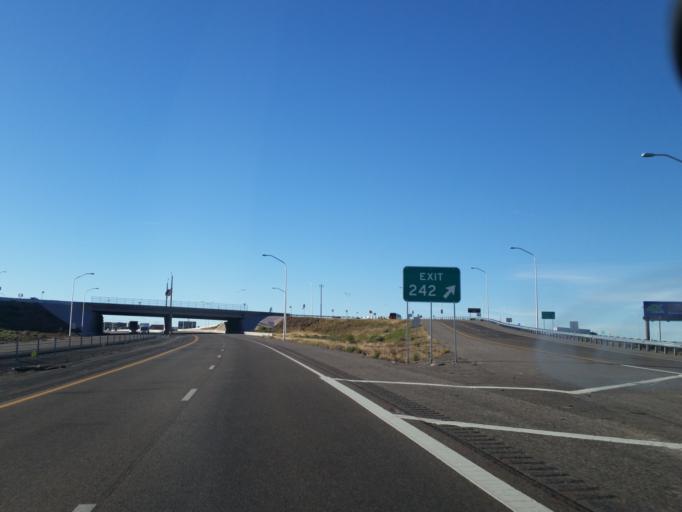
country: US
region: New Mexico
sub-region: Sandoval County
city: Bernalillo
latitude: 35.3188
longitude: -106.5332
